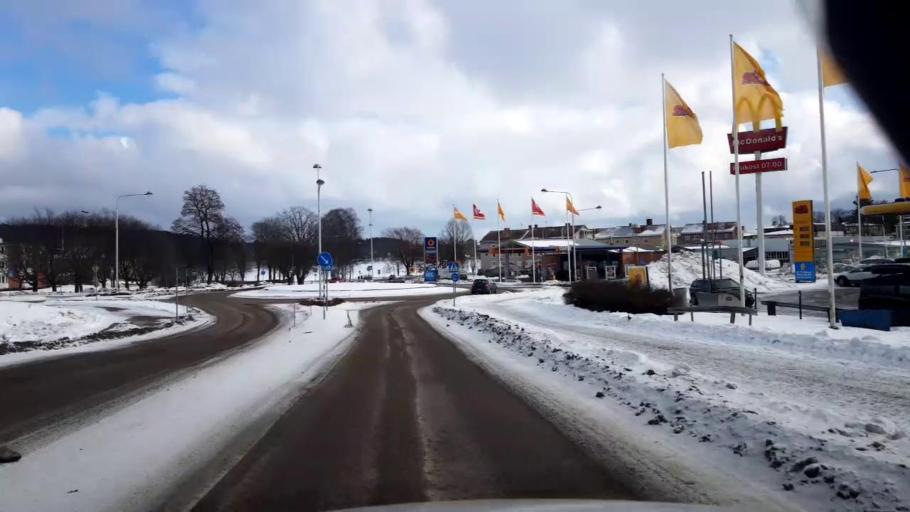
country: SE
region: Gaevleborg
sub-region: Hudiksvalls Kommun
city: Hudiksvall
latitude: 61.7345
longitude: 17.0992
